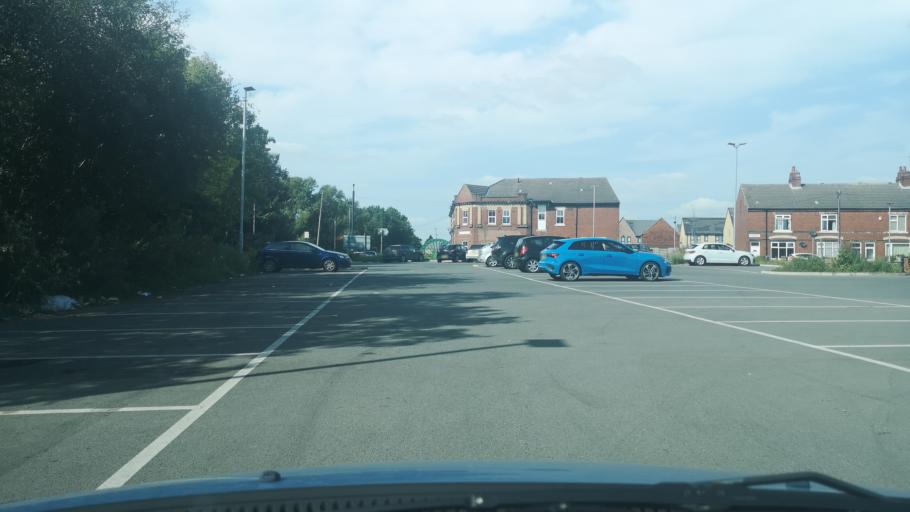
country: GB
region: England
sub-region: City and Borough of Wakefield
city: Fitzwilliam
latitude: 53.6321
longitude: -1.3727
